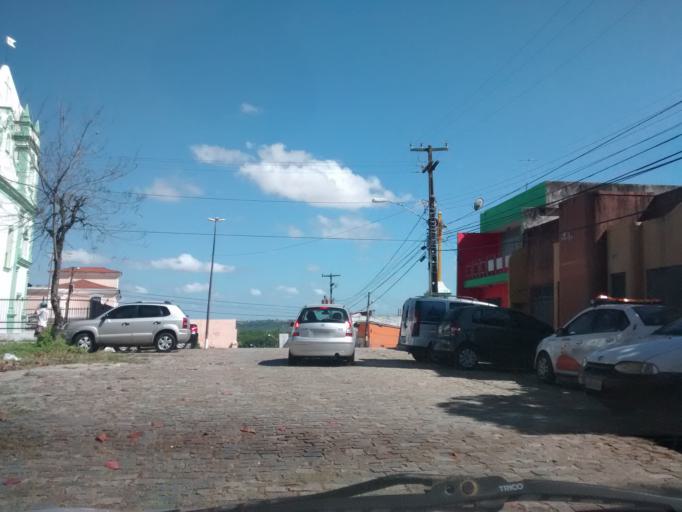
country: BR
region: Rio Grande do Norte
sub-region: Natal
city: Natal
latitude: -5.7833
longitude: -35.2083
